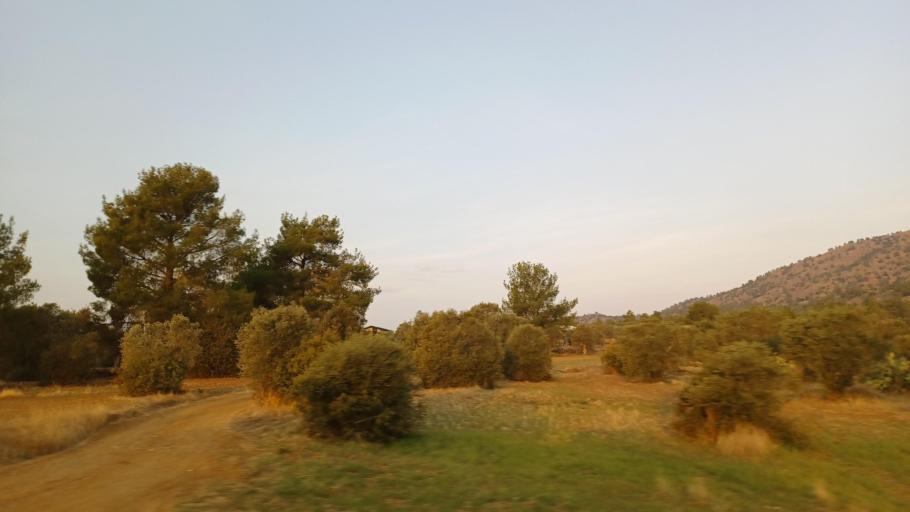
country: CY
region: Larnaka
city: Kornos
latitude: 34.9234
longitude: 33.3901
